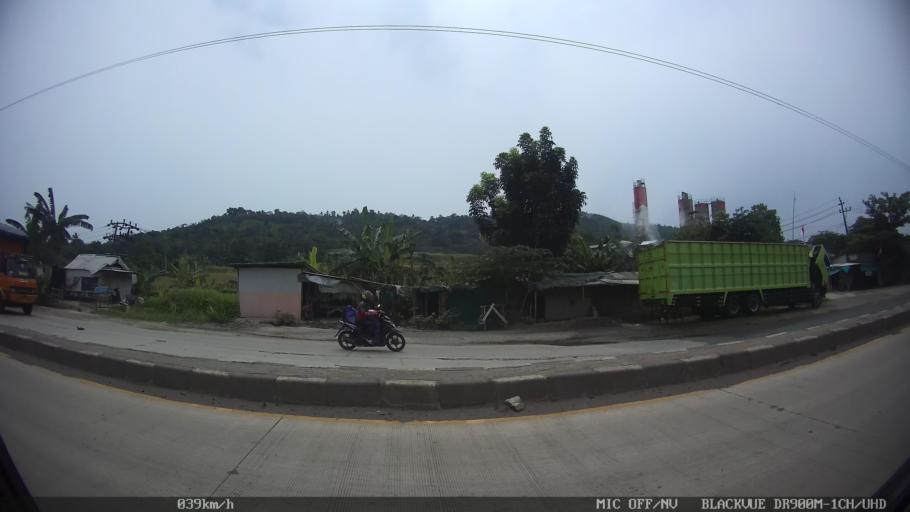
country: ID
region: Lampung
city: Bandarlampung
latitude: -5.4266
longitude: 105.2961
